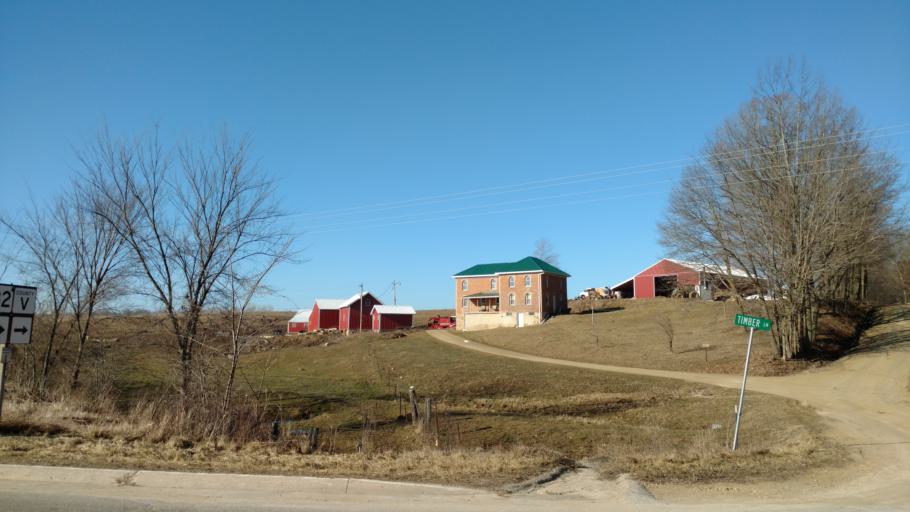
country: US
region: Wisconsin
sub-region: Vernon County
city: Hillsboro
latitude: 43.6327
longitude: -90.4524
